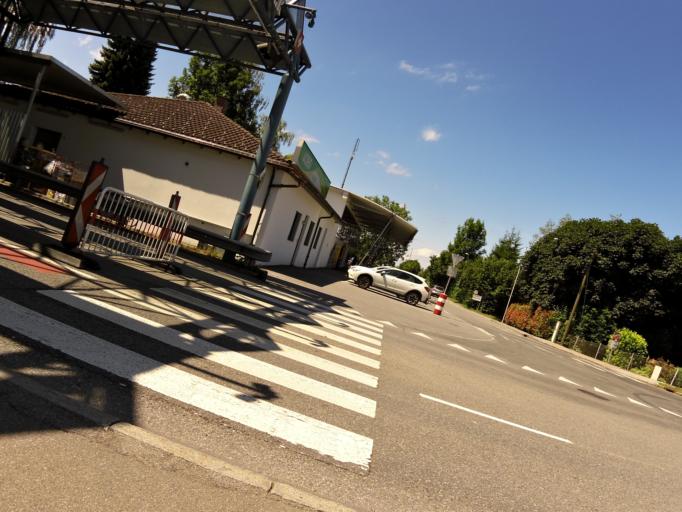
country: AT
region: Vorarlberg
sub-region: Politischer Bezirk Bregenz
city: Gaissau
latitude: 47.4644
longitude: 9.5958
